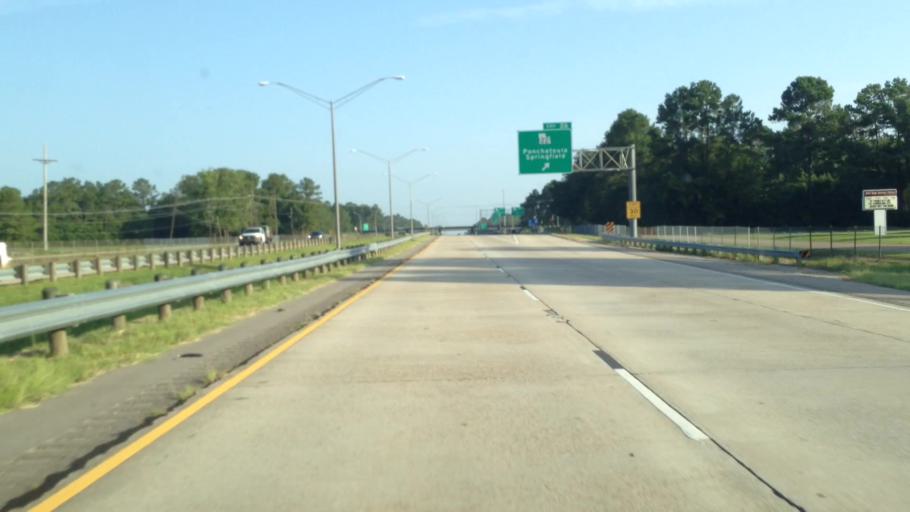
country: US
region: Louisiana
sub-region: Tangipahoa Parish
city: Ponchatoula
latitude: 30.4342
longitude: -90.4575
